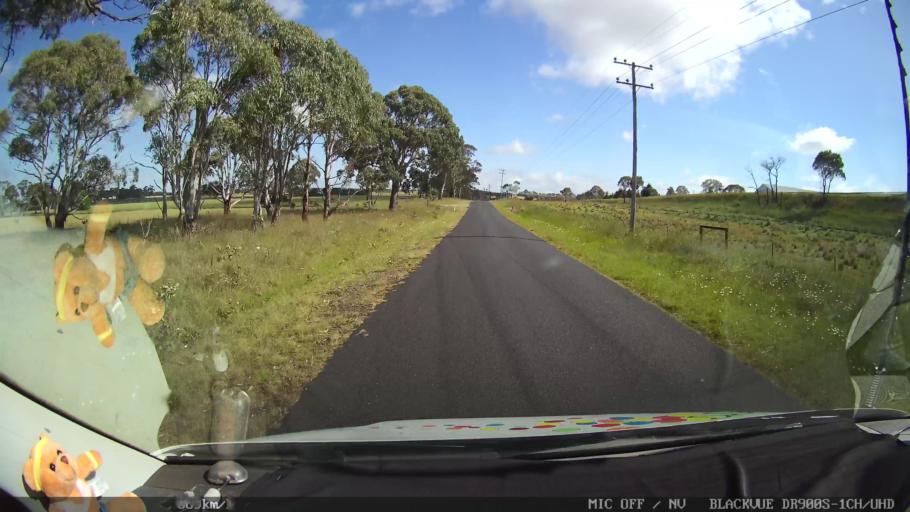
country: AU
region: New South Wales
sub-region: Guyra
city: Guyra
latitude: -30.1949
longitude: 151.6761
